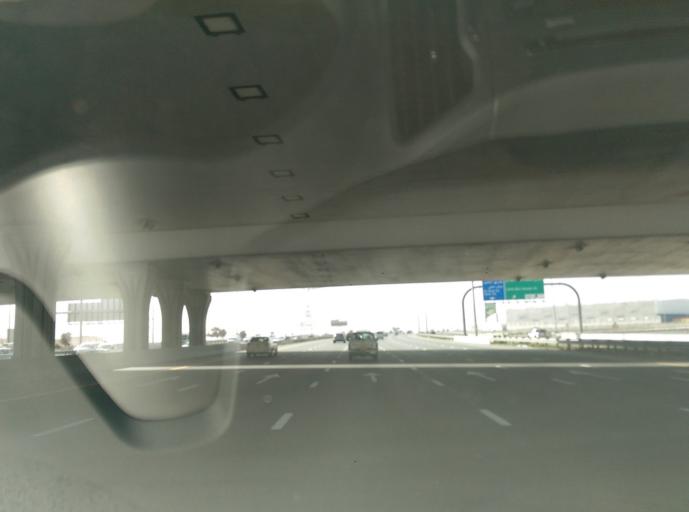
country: AE
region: Dubai
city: Dubai
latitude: 25.1448
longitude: 55.2610
